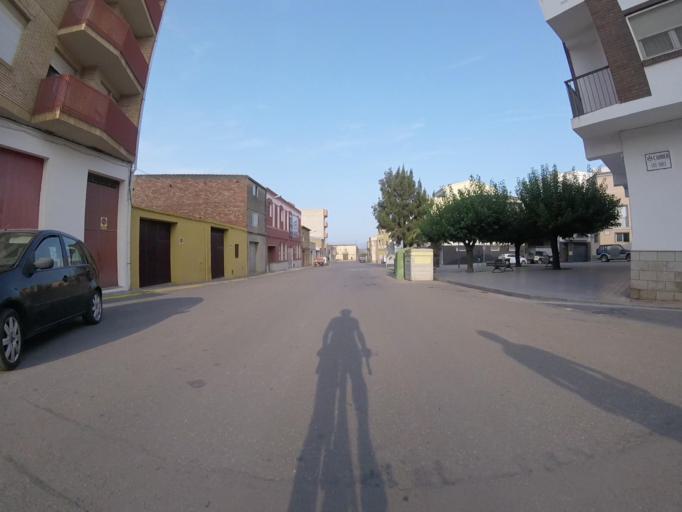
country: ES
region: Valencia
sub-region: Provincia de Castello
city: Cabanes
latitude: 40.1544
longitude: 0.0413
